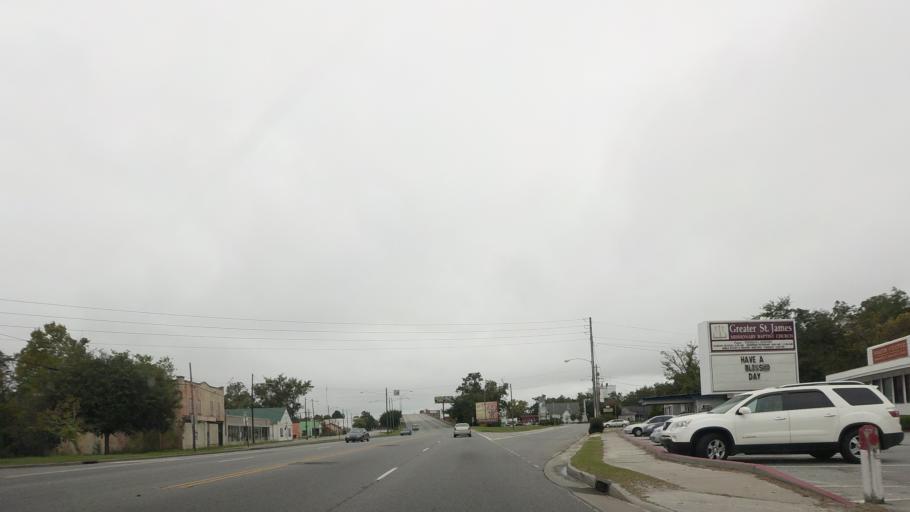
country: US
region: Georgia
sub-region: Lowndes County
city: Valdosta
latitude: 30.8247
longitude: -83.2755
